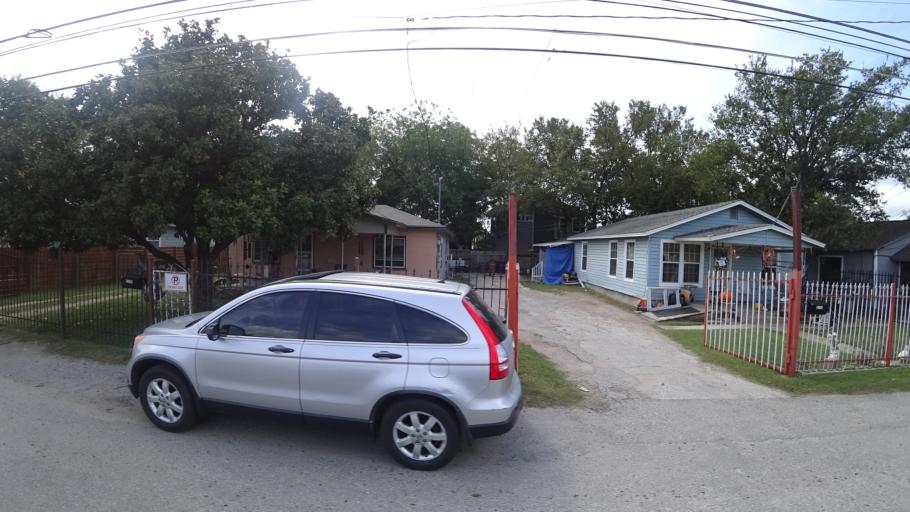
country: US
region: Texas
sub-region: Travis County
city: Austin
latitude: 30.2586
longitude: -97.7168
